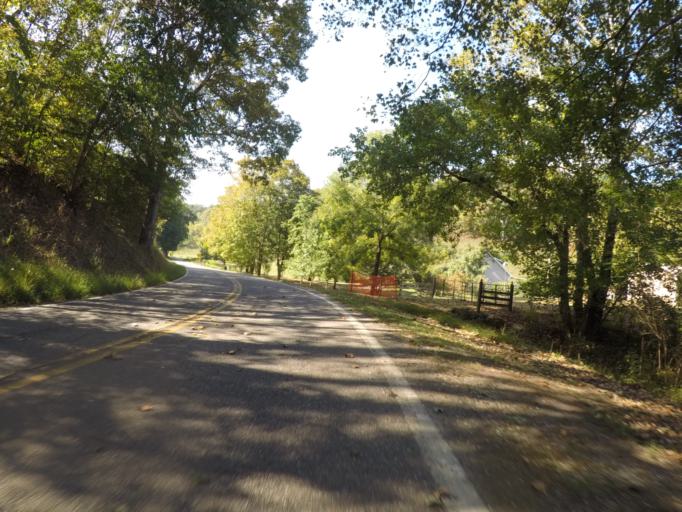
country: US
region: West Virginia
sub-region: Cabell County
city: Lesage
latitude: 38.6417
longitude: -82.4317
